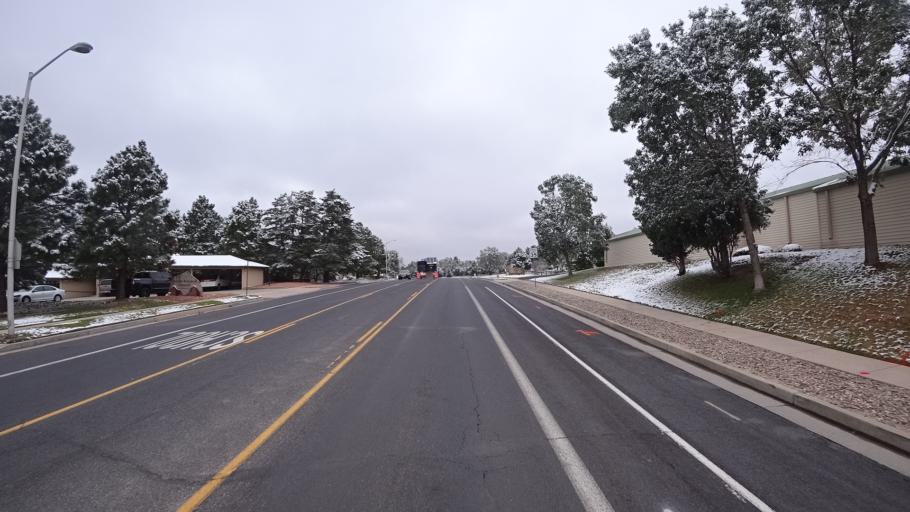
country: US
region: Colorado
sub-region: El Paso County
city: Cimarron Hills
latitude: 38.9163
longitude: -104.7641
